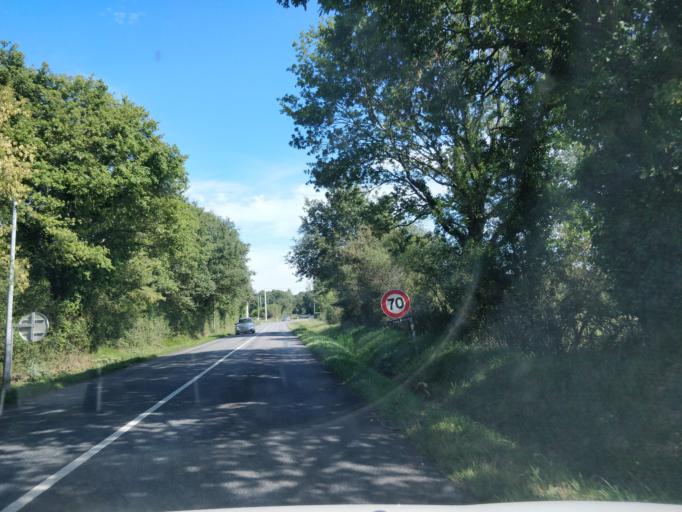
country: FR
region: Pays de la Loire
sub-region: Departement de la Loire-Atlantique
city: Quilly
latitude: 47.4562
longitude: -1.9236
